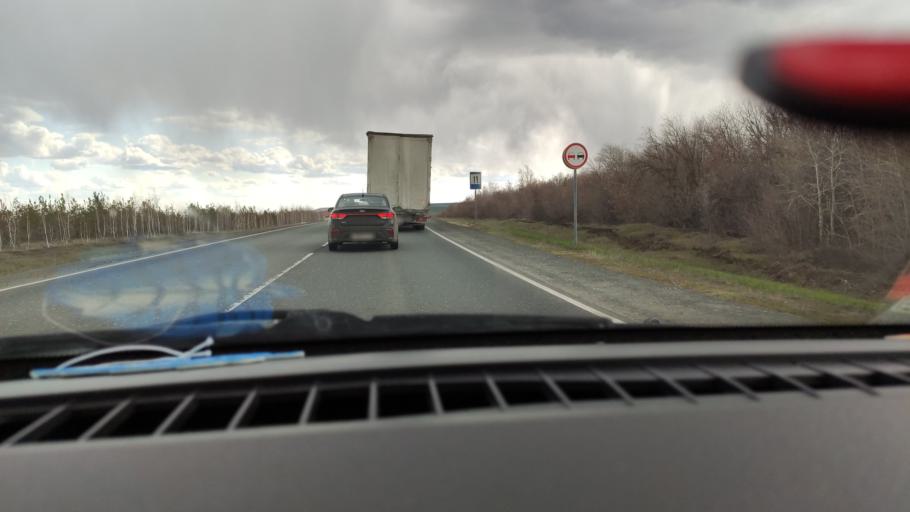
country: RU
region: Saratov
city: Balakovo
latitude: 52.1596
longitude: 47.8204
